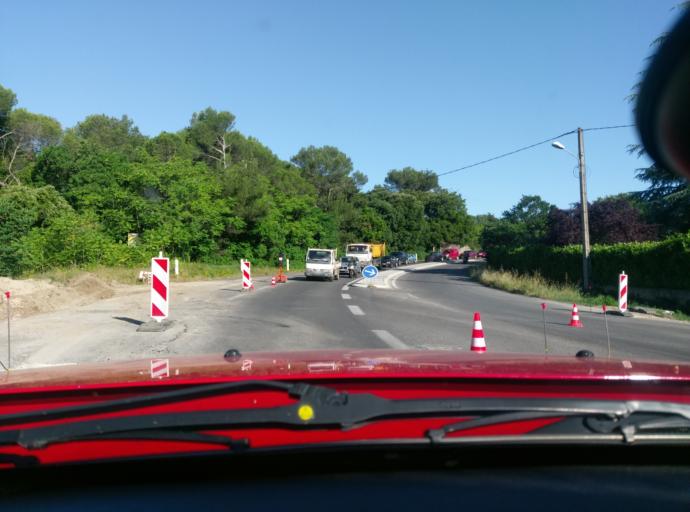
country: FR
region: Languedoc-Roussillon
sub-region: Departement du Gard
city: Uzes
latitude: 43.9928
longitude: 4.4201
